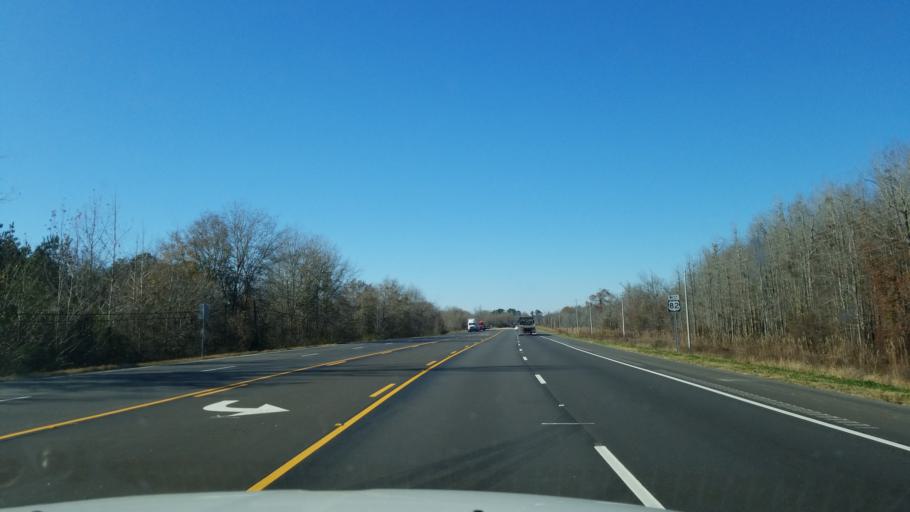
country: US
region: Alabama
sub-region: Pickens County
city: Reform
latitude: 33.3725
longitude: -88.0001
